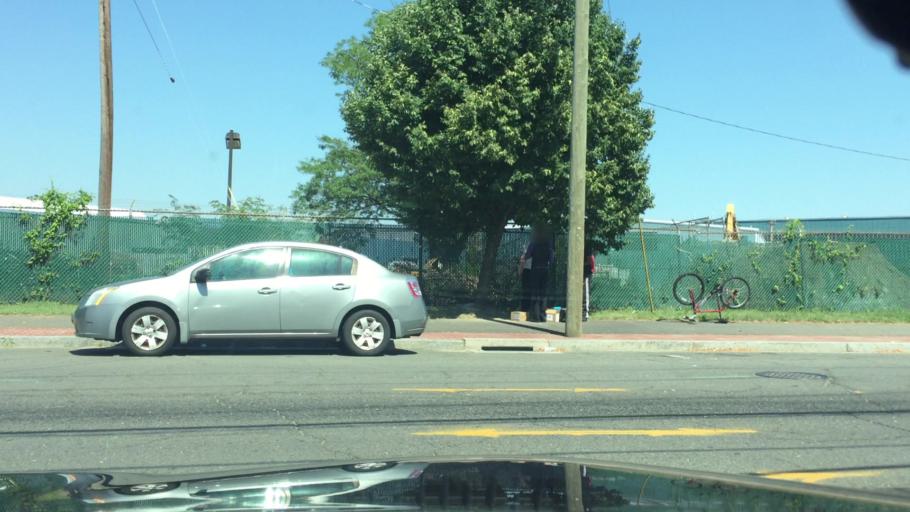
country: US
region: Connecticut
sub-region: Fairfield County
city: Bridgeport
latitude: 41.1934
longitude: -73.1934
